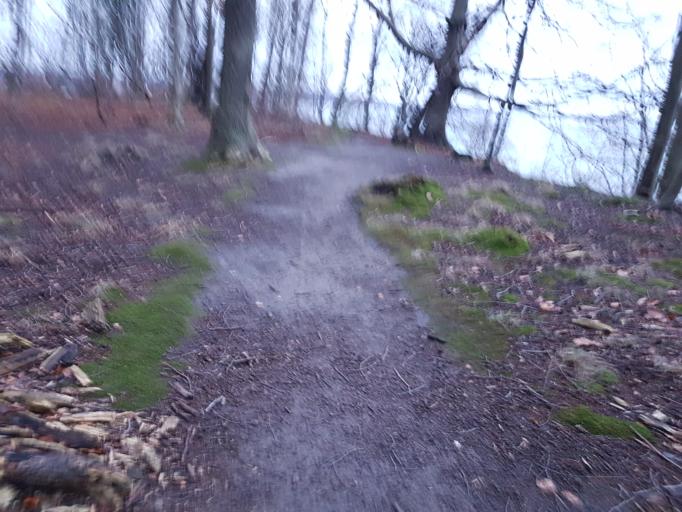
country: DE
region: Mecklenburg-Vorpommern
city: Ostseebad Binz
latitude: 54.3996
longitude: 13.6348
